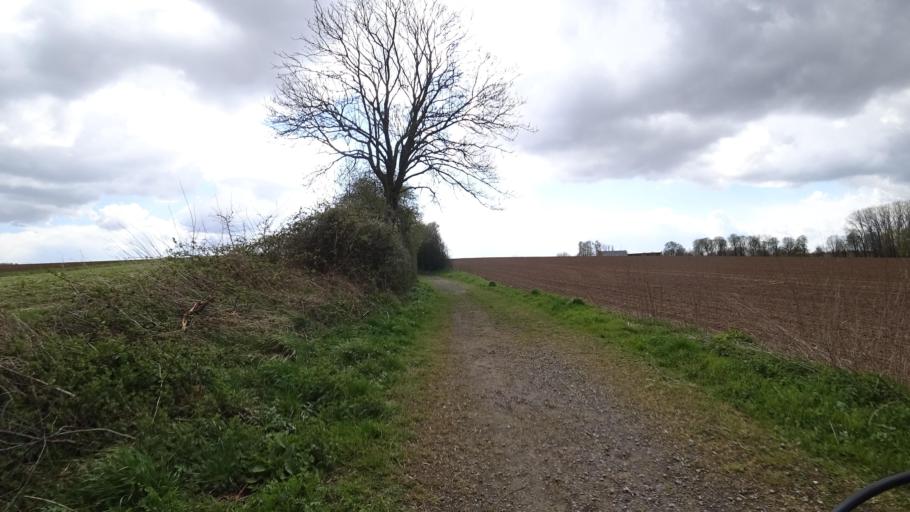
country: BE
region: Wallonia
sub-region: Province du Brabant Wallon
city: Walhain-Saint-Paul
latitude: 50.6358
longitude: 4.7273
